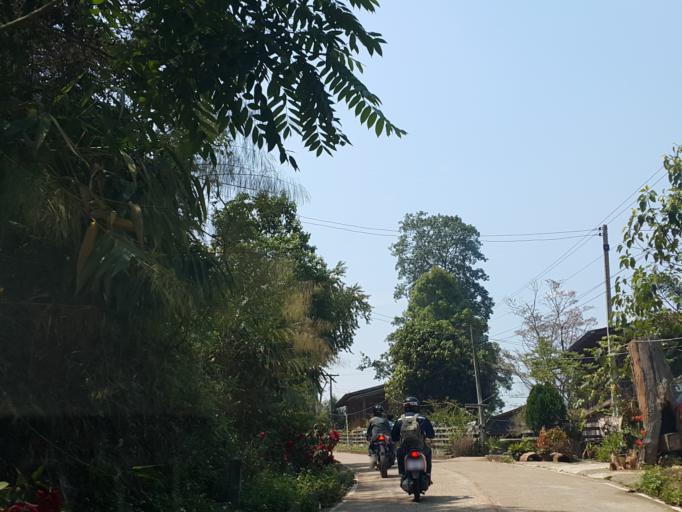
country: TH
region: Lampang
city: Mueang Pan
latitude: 18.8247
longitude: 99.3867
